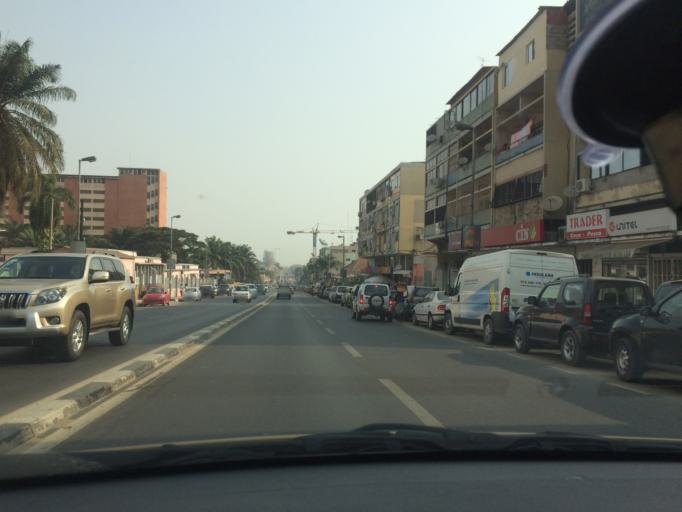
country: AO
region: Luanda
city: Luanda
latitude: -8.8256
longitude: 13.2243
